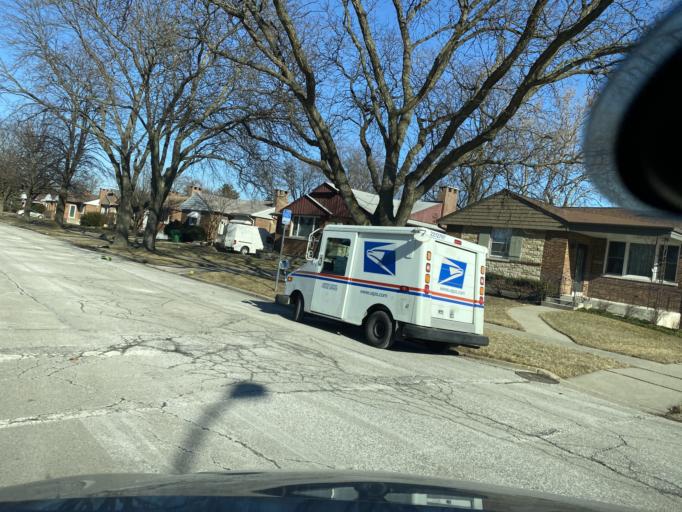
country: US
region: Illinois
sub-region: Cook County
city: Westchester
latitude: 41.8562
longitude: -87.8736
